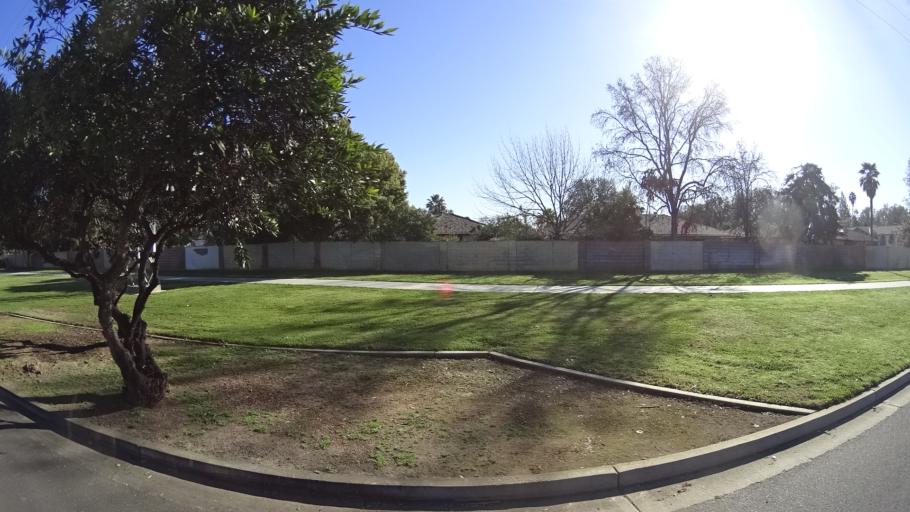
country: US
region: California
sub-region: Fresno County
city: Clovis
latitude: 36.8397
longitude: -119.7703
